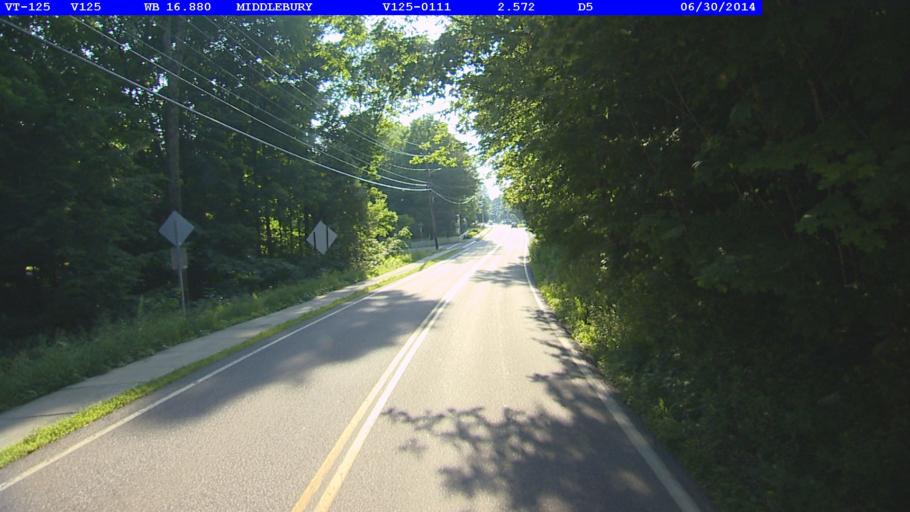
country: US
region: Vermont
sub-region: Addison County
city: Middlebury (village)
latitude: 43.9710
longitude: -73.0907
